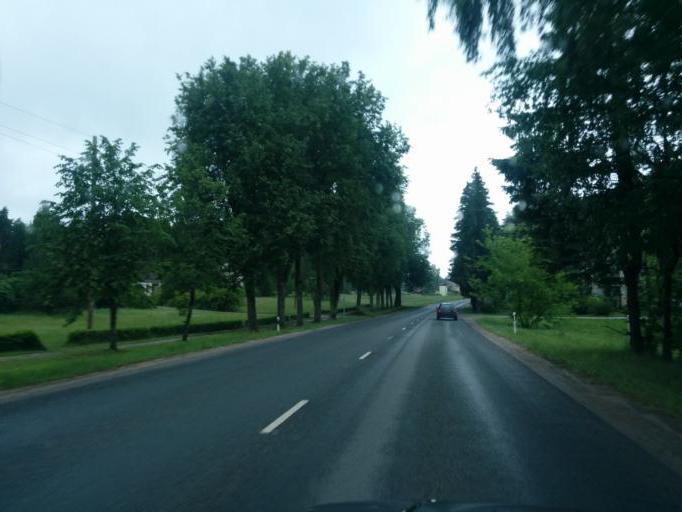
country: LV
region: Smiltene
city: Smiltene
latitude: 57.4100
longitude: 25.9394
